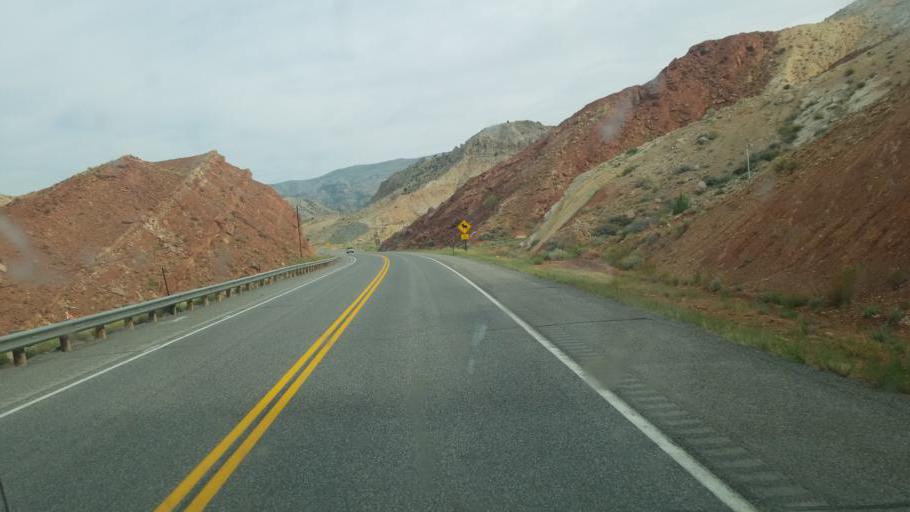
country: US
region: Wyoming
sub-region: Hot Springs County
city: Thermopolis
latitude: 43.4001
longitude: -108.1646
